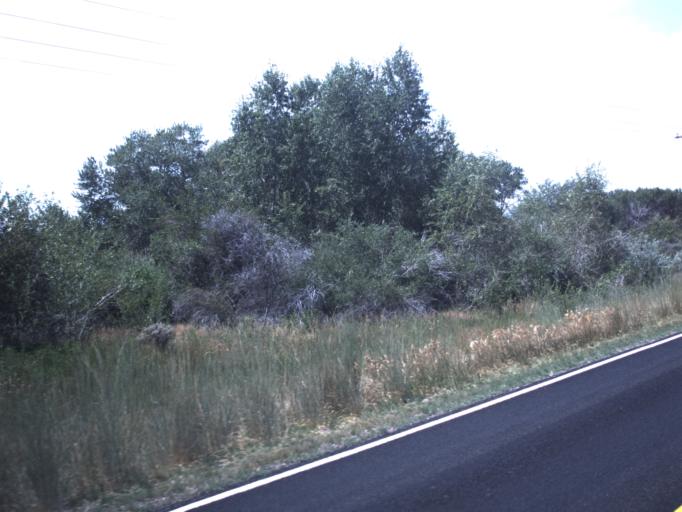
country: US
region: Utah
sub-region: Duchesne County
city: Roosevelt
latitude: 40.4199
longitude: -109.9213
